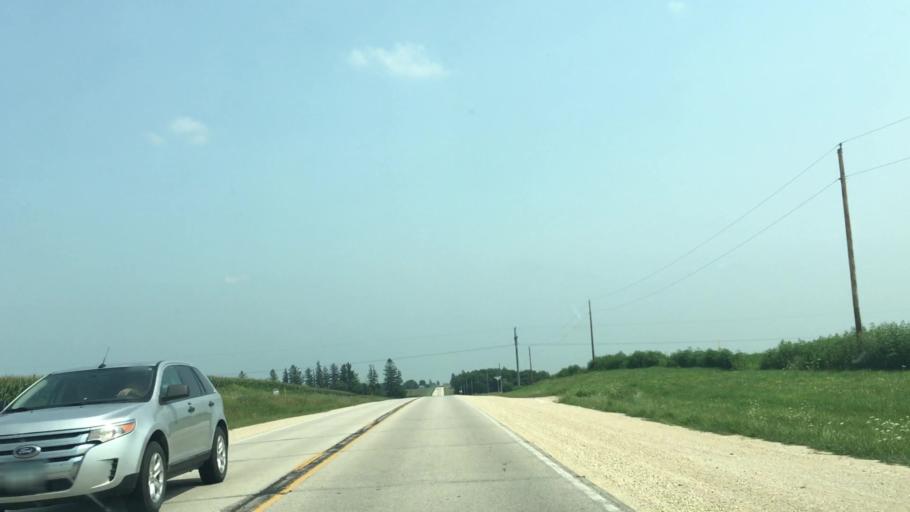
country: US
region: Iowa
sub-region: Fayette County
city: Oelwein
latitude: 42.6798
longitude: -91.8570
